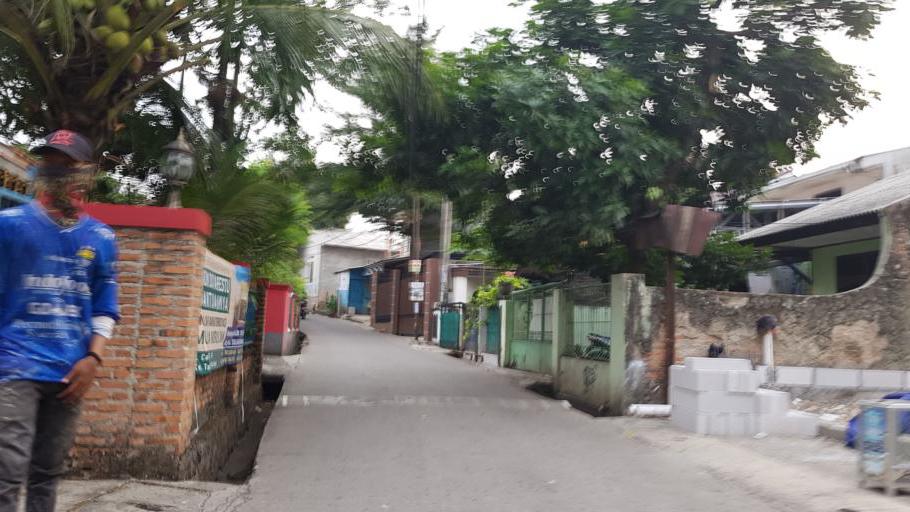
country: ID
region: West Java
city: Depok
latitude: -6.3814
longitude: 106.8049
